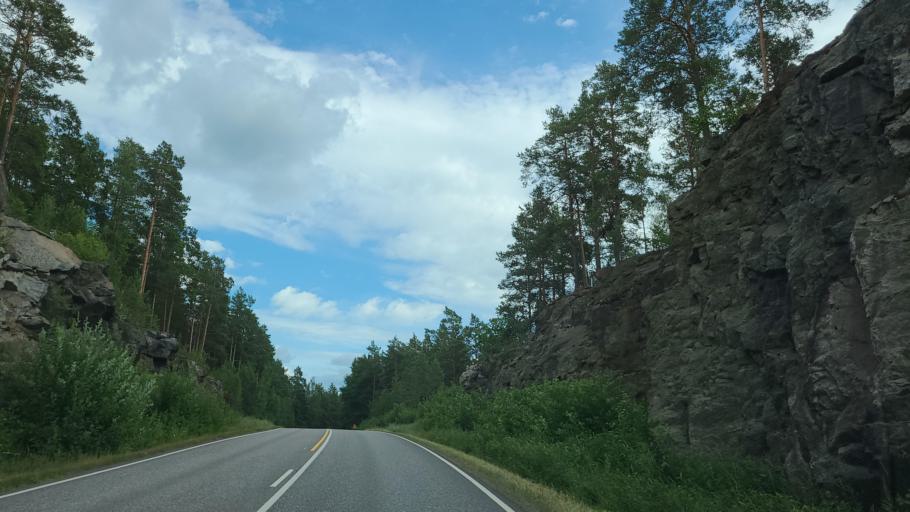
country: FI
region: Varsinais-Suomi
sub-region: Turku
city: Rymaettylae
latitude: 60.3636
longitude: 21.9498
